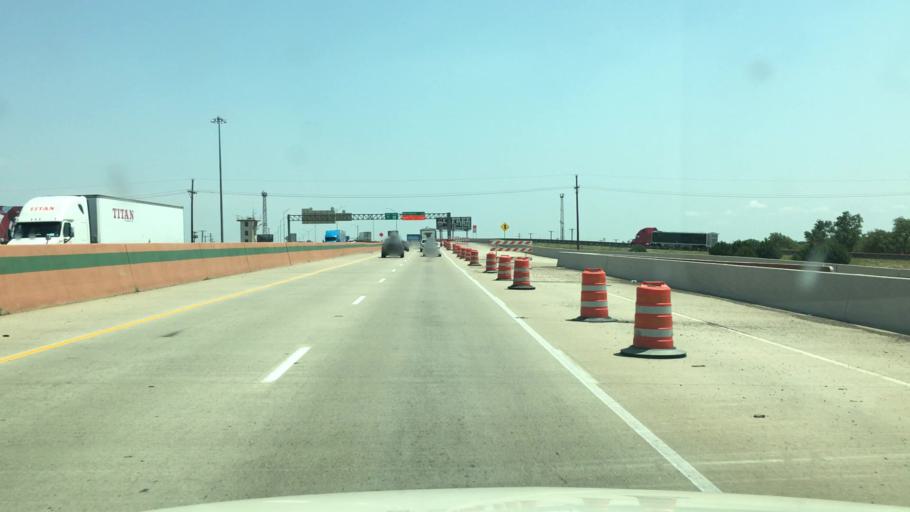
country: US
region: Texas
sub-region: Potter County
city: Amarillo
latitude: 35.1927
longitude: -101.8358
